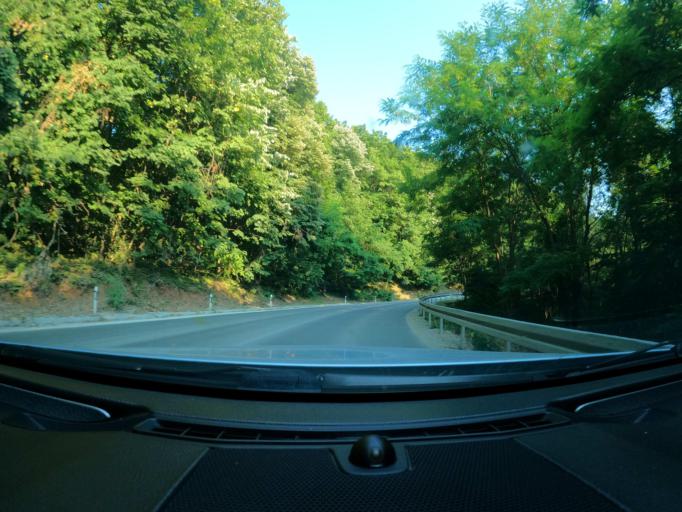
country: RS
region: Autonomna Pokrajina Vojvodina
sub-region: Juznobacki Okrug
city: Beocin
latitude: 45.1585
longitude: 19.7151
